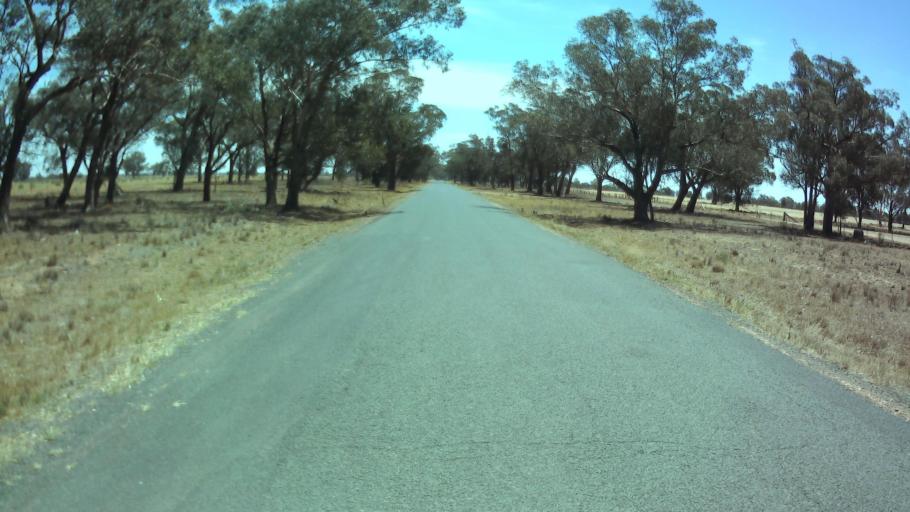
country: AU
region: New South Wales
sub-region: Weddin
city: Grenfell
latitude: -34.0003
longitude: 147.7447
